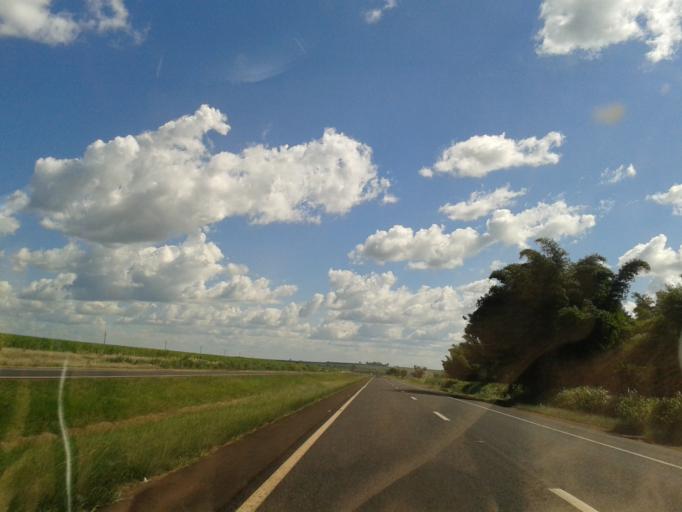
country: BR
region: Goias
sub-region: Morrinhos
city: Morrinhos
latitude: -17.8590
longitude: -49.2229
